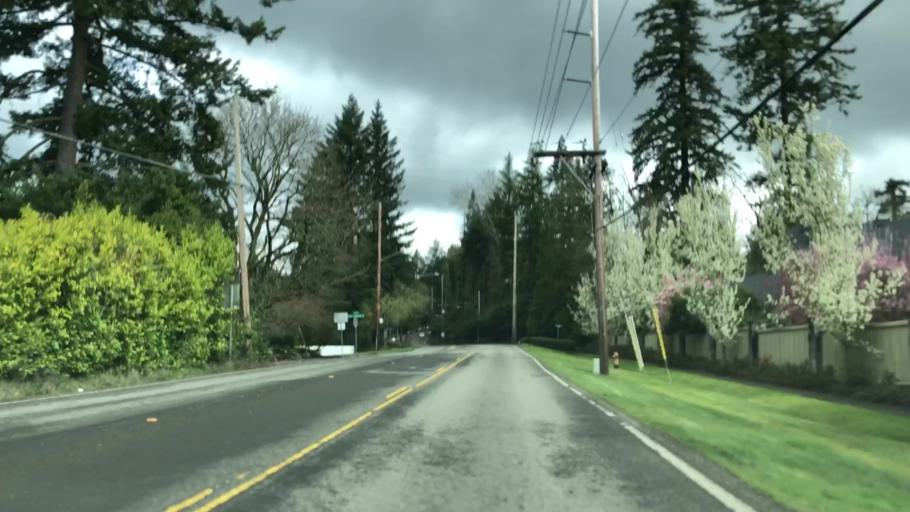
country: US
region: Oregon
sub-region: Washington County
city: Raleigh Hills
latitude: 45.4922
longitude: -122.7439
